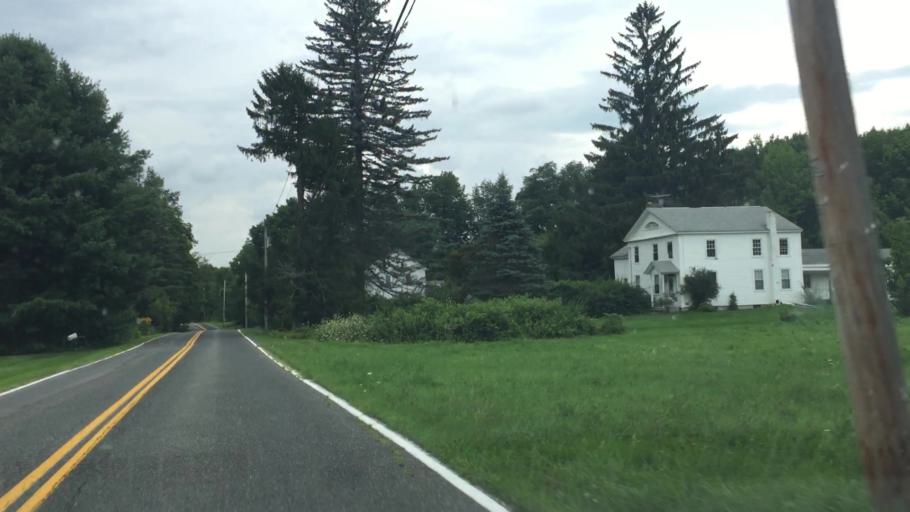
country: US
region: Massachusetts
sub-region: Berkshire County
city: West Stockbridge
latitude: 42.3047
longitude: -73.4022
